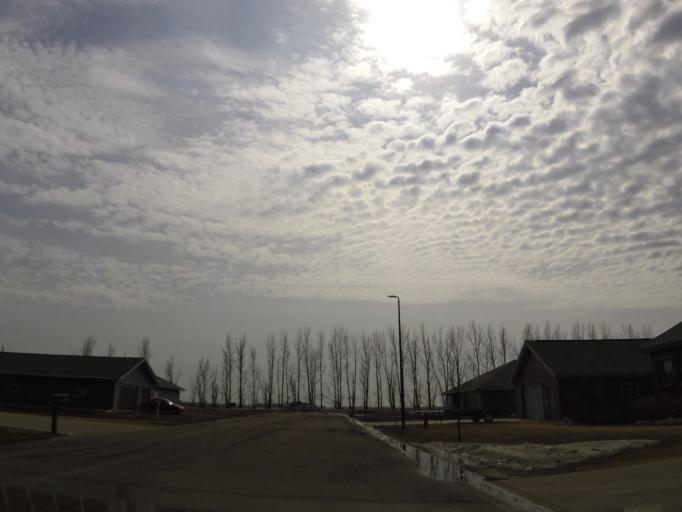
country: US
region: North Dakota
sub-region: Walsh County
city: Grafton
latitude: 48.4062
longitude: -97.4279
